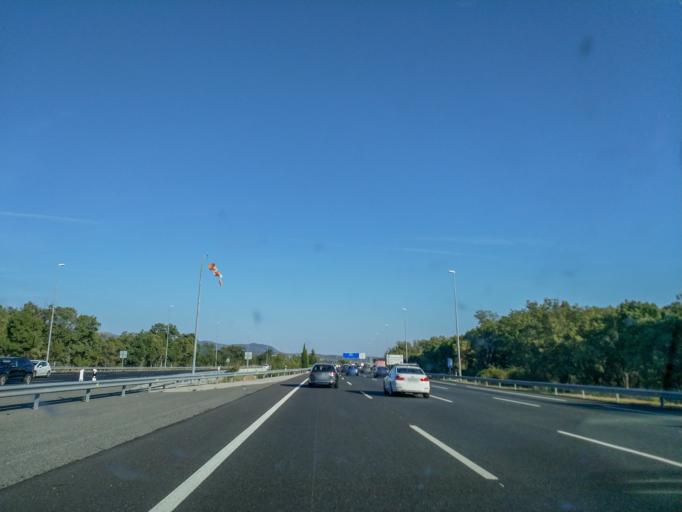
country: ES
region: Madrid
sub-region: Provincia de Madrid
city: Alpedrete
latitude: 40.6475
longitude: -4.0550
